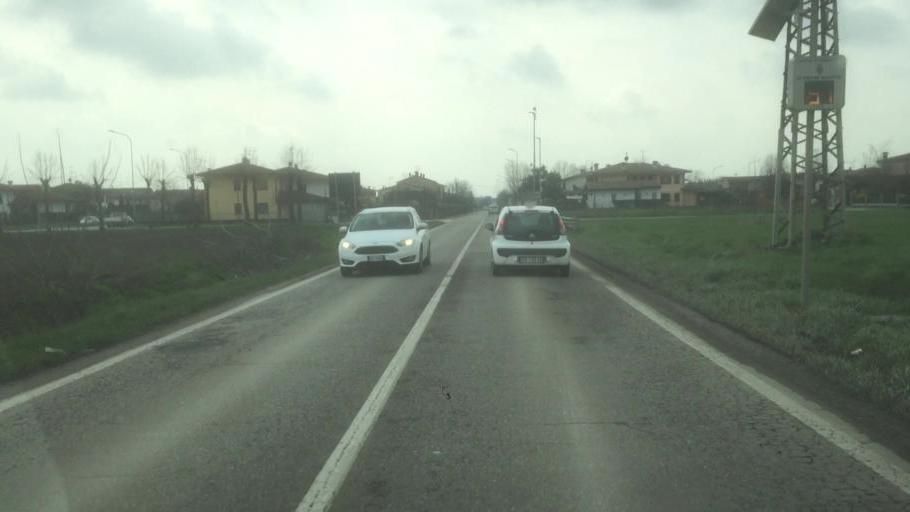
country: IT
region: Lombardy
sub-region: Provincia di Mantova
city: Casaloldo
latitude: 45.2599
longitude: 10.4765
